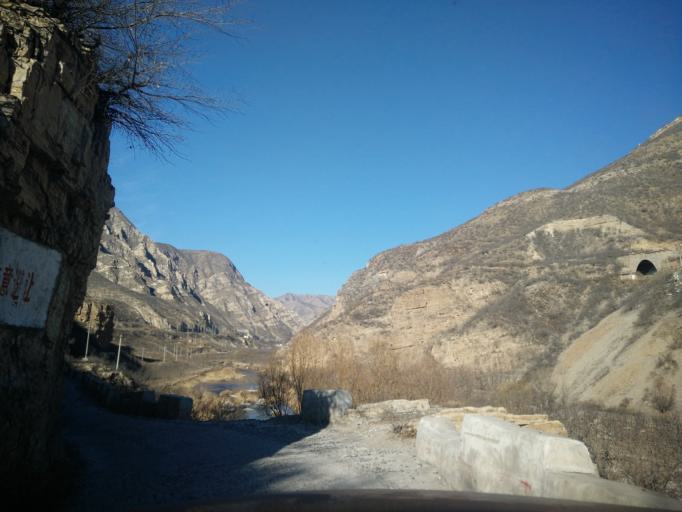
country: CN
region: Beijing
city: Yanjiatai
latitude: 40.1653
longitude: 115.6469
